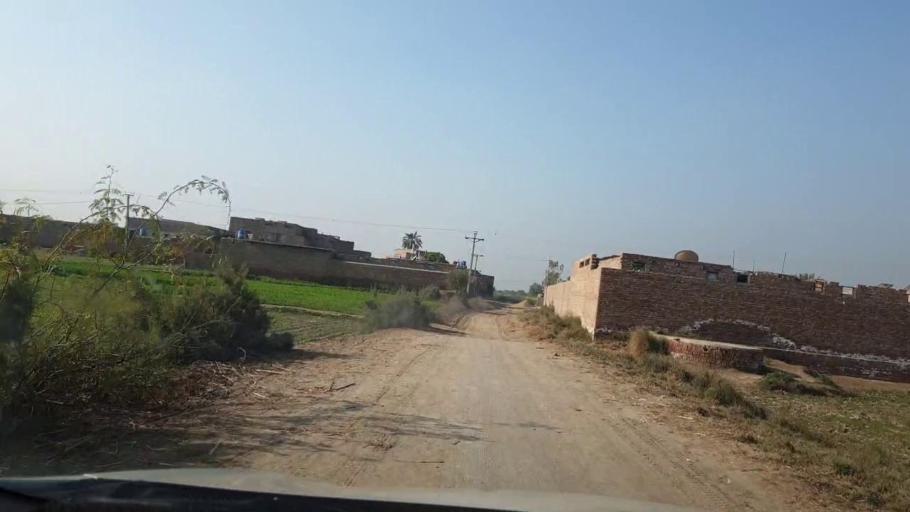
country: PK
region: Sindh
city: Matiari
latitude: 25.6848
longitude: 68.5388
